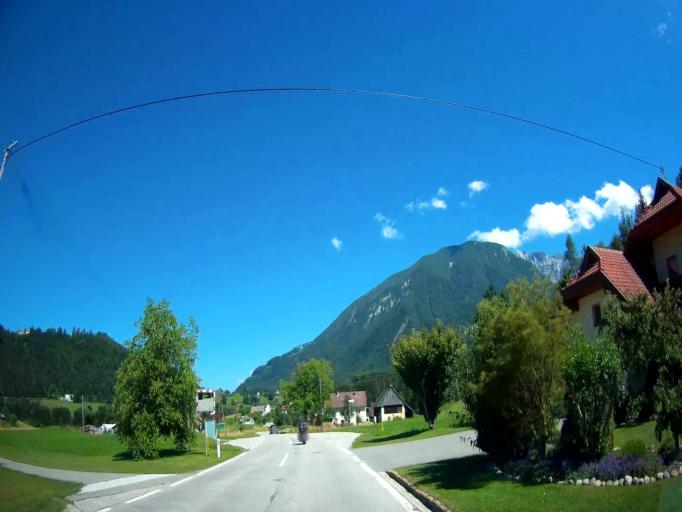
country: AT
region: Carinthia
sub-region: Politischer Bezirk Klagenfurt Land
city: Grafenstein
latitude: 46.5393
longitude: 14.4359
